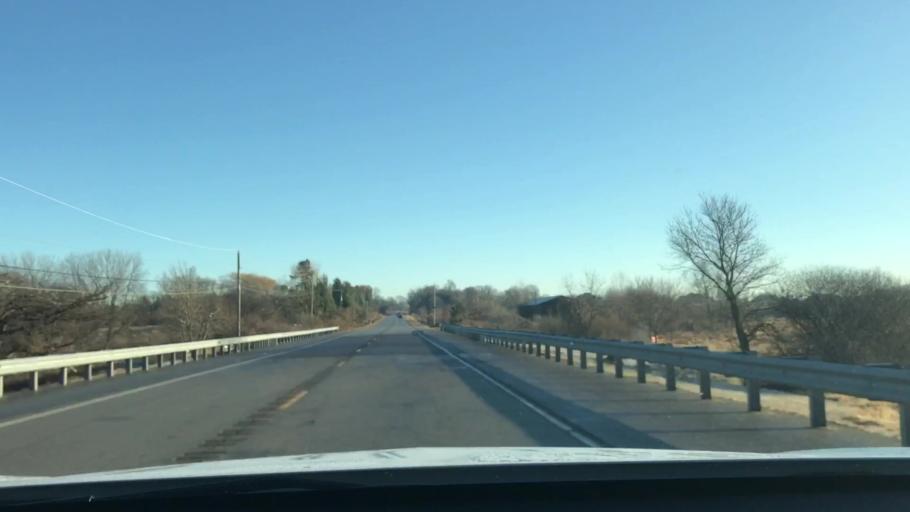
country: US
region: Illinois
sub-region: Kane County
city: Pingree Grove
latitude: 42.0940
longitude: -88.4141
